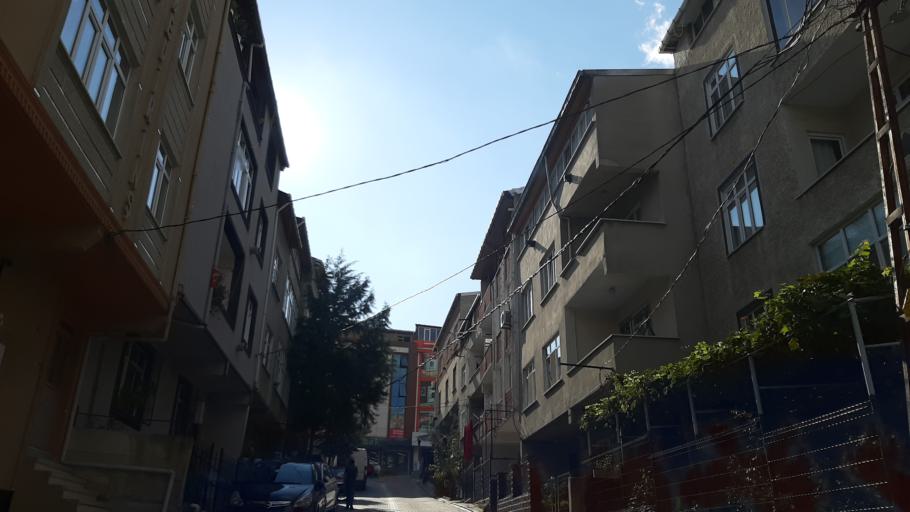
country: TR
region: Istanbul
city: Esenyurt
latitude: 41.0370
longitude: 28.6565
